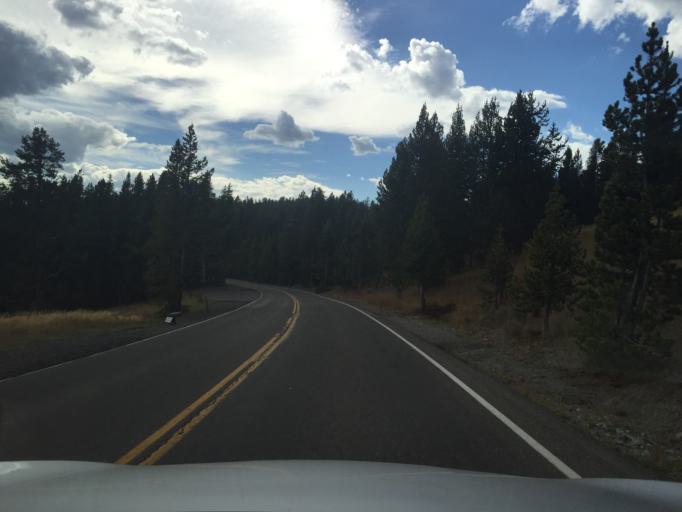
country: US
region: Montana
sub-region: Gallatin County
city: West Yellowstone
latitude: 44.7200
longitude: -110.5027
